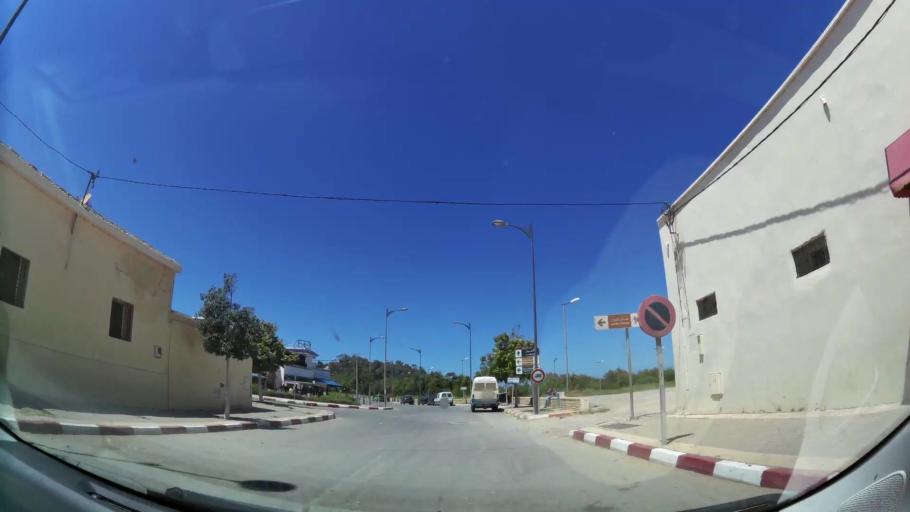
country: MA
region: Oriental
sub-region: Berkane-Taourirt
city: Madagh
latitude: 35.0806
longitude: -2.2135
